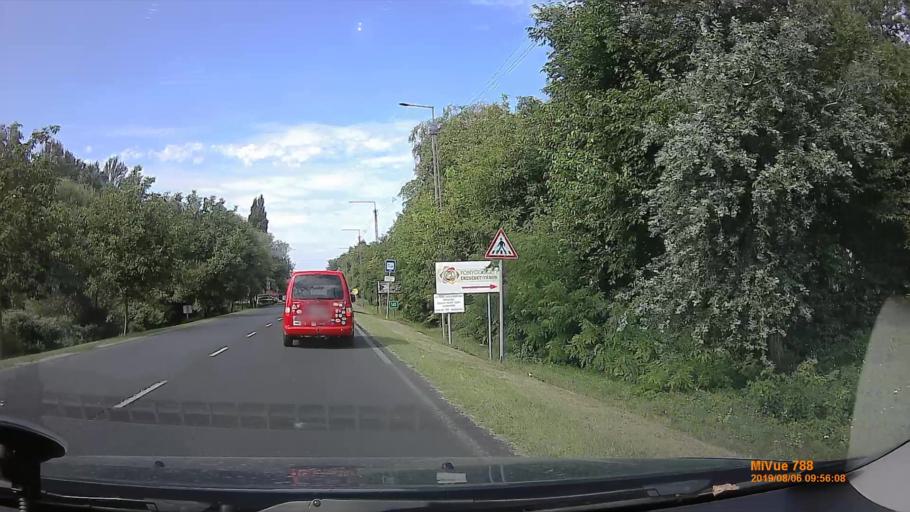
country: HU
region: Somogy
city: Fonyod
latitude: 46.7588
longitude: 17.5946
